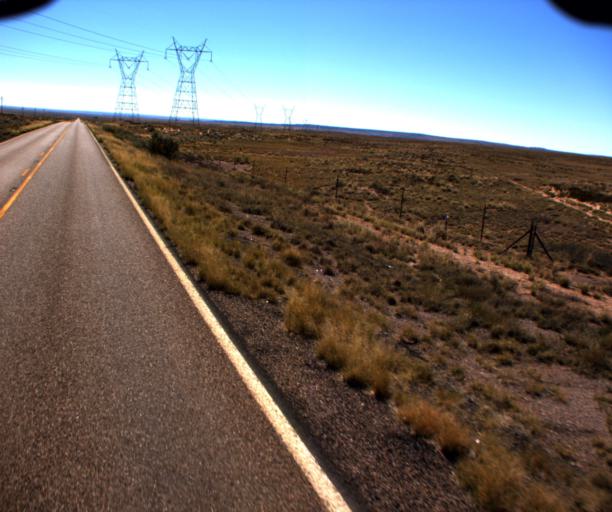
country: US
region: Arizona
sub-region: Navajo County
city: Holbrook
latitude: 35.1636
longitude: -110.0807
